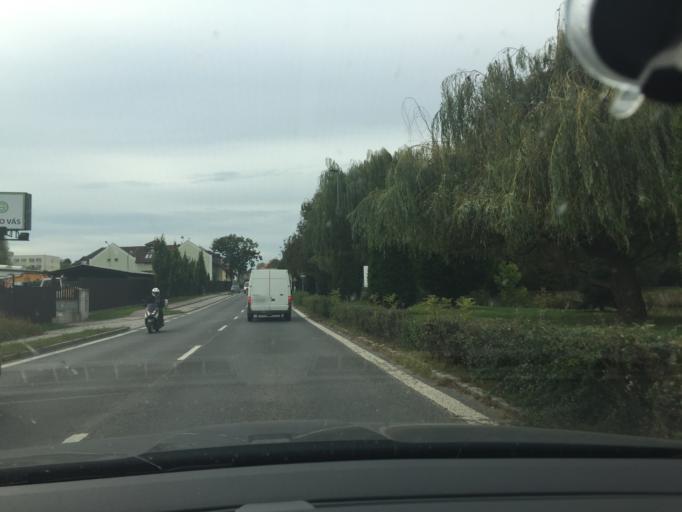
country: CZ
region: Praha
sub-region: Praha 20
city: Horni Pocernice
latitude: 50.1182
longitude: 14.6336
